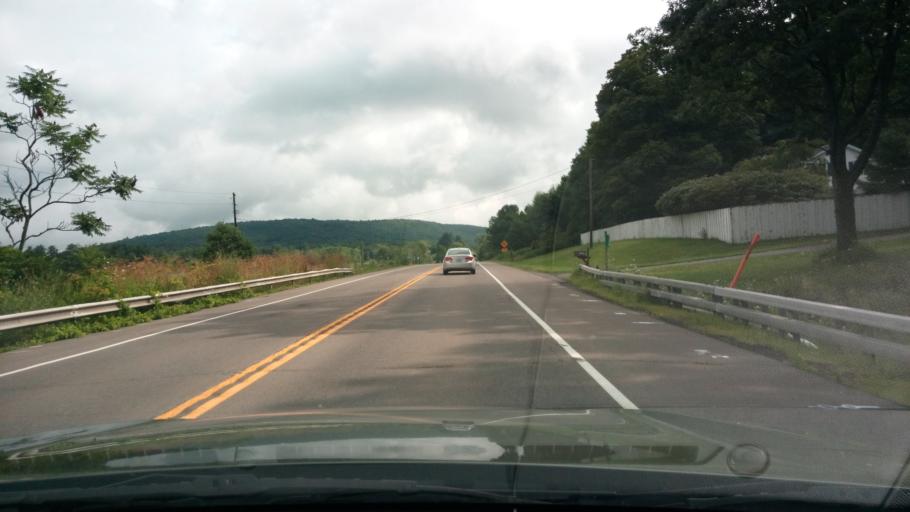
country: US
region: New York
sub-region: Tompkins County
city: Northwest Ithaca
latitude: 42.3428
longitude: -76.6237
